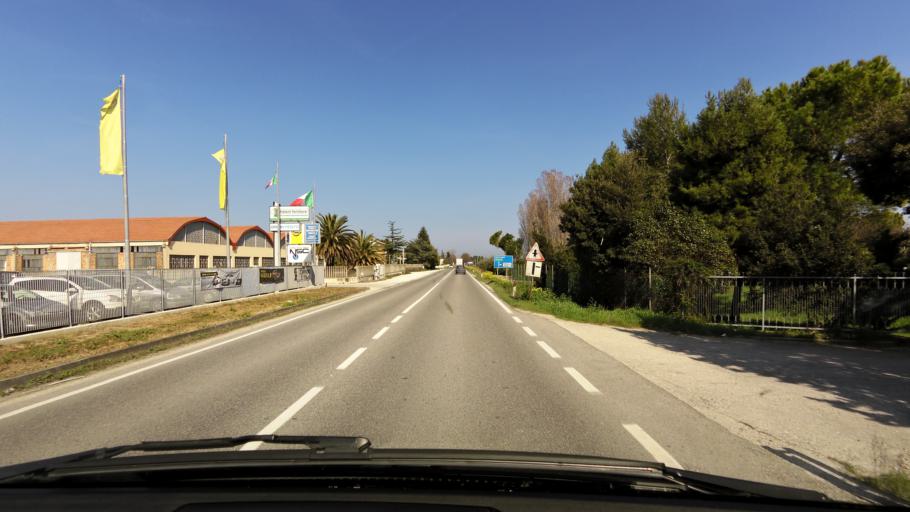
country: IT
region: The Marches
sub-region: Provincia di Macerata
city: Potenza Picena
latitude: 43.3943
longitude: 13.6428
